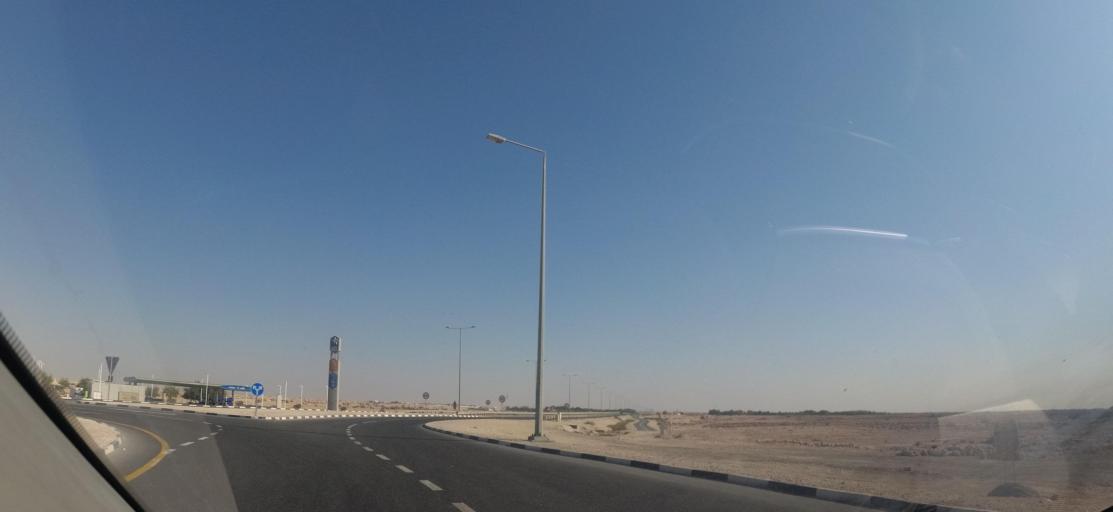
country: QA
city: Al Jumayliyah
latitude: 25.6172
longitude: 51.0842
